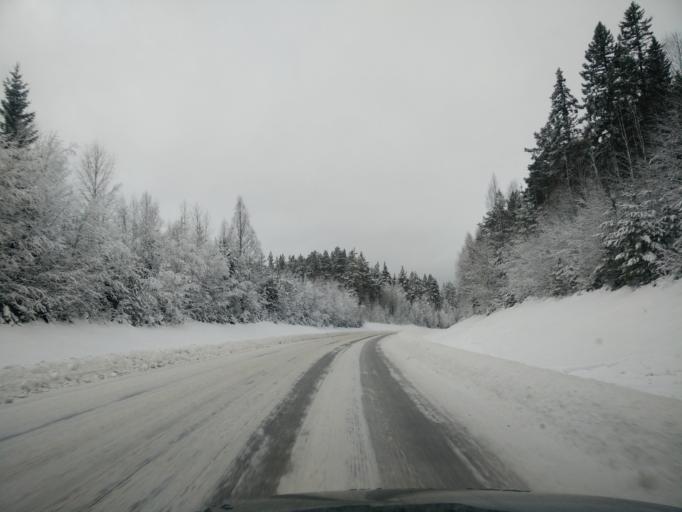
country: SE
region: Vaesternorrland
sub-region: Ange Kommun
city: Ange
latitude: 62.4021
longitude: 15.4793
